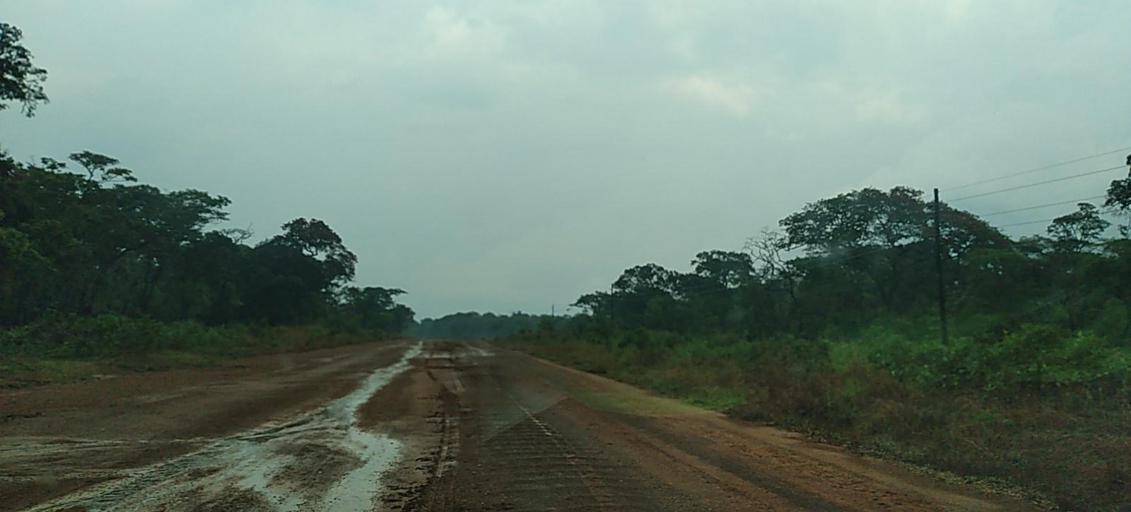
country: ZM
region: North-Western
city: Mwinilunga
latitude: -11.5840
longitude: 24.3887
